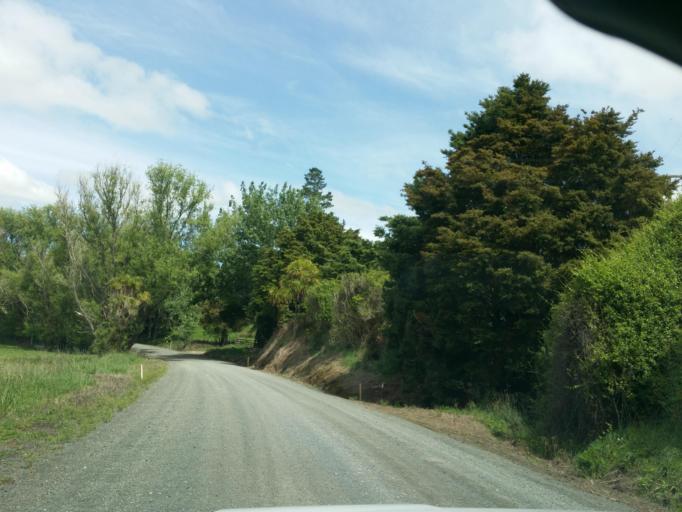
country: NZ
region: Northland
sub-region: Whangarei
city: Maungatapere
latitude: -35.9021
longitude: 174.1428
